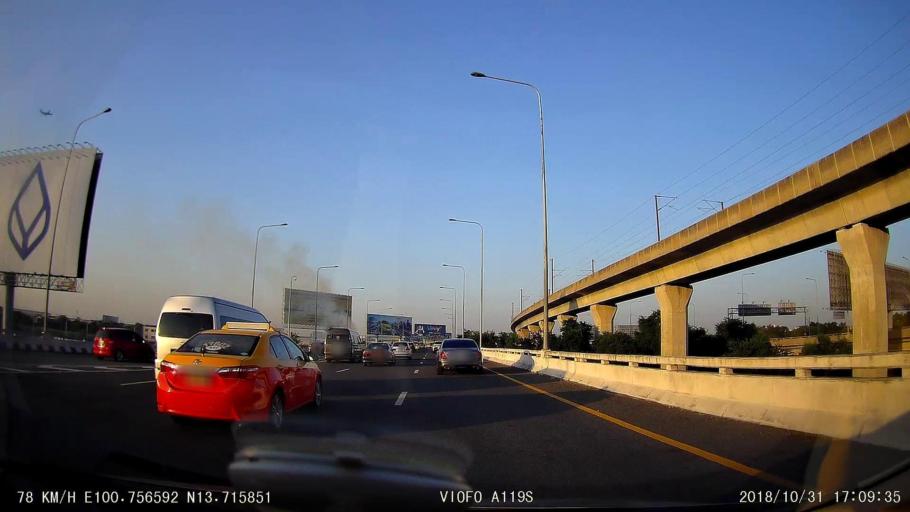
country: TH
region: Bangkok
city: Lat Krabang
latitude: 13.7160
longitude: 100.7567
